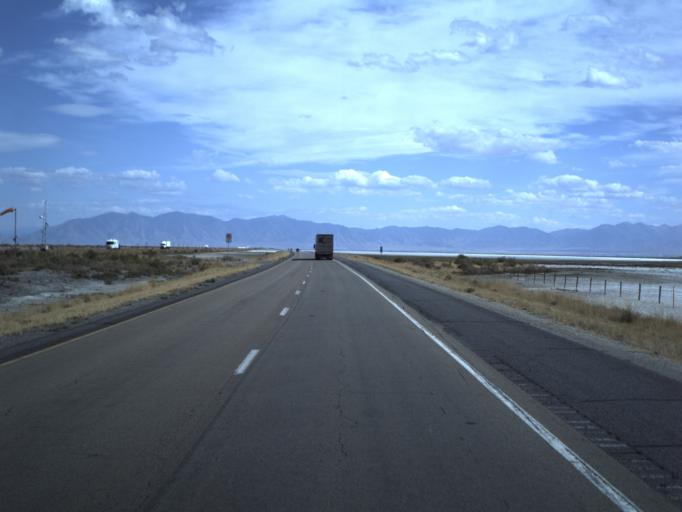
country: US
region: Utah
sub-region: Tooele County
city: Grantsville
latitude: 40.7404
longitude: -112.6249
